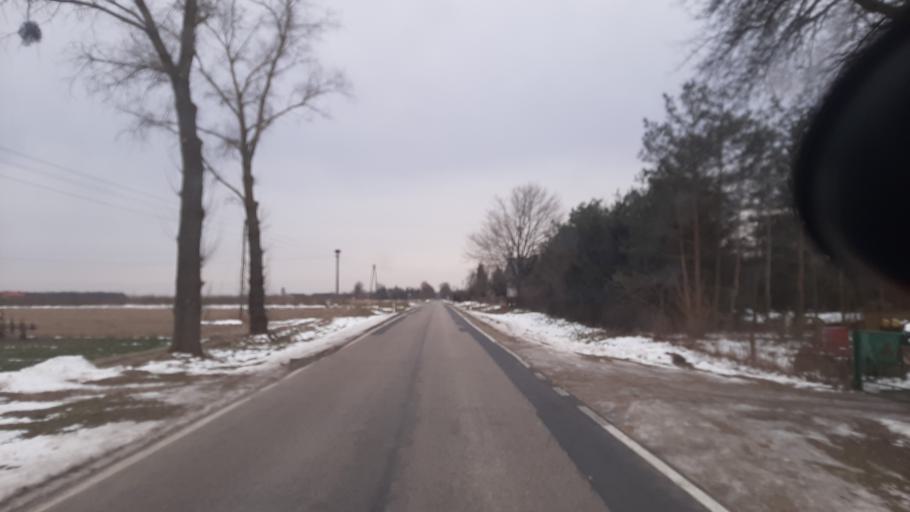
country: PL
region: Lublin Voivodeship
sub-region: Powiat lubartowski
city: Kamionka
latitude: 51.4655
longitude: 22.4200
